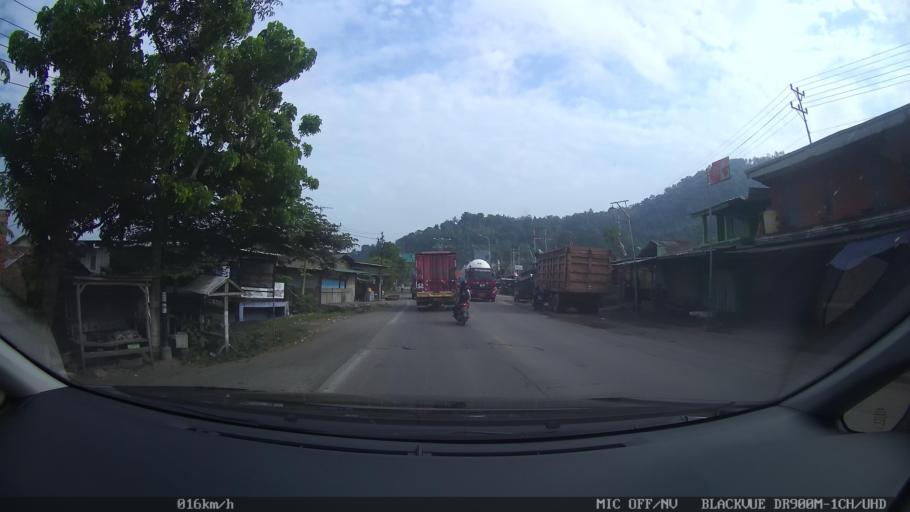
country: ID
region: Lampung
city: Panjang
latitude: -5.4637
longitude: 105.3215
